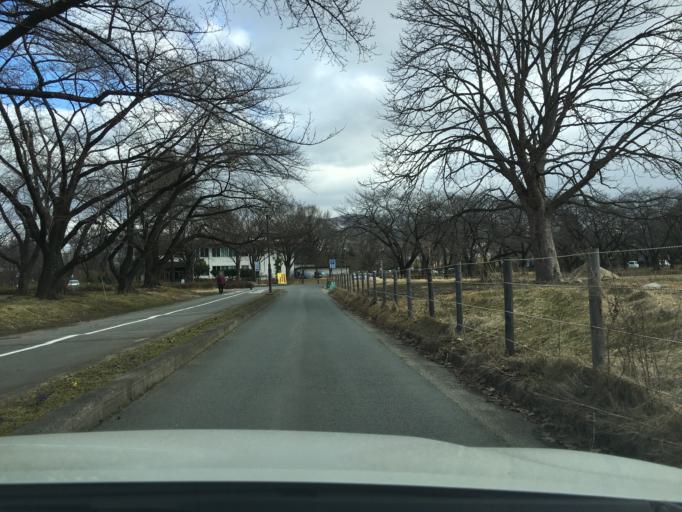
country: JP
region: Yamagata
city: Yamagata-shi
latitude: 38.2573
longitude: 140.3293
